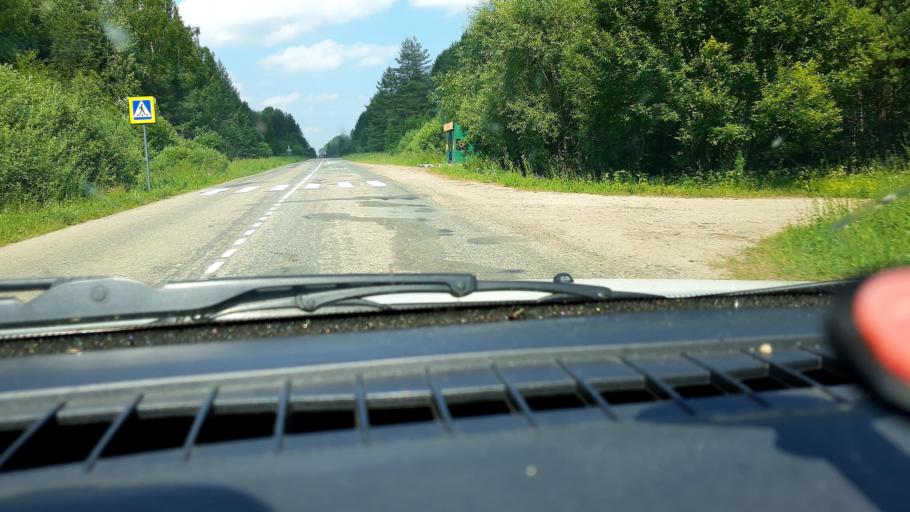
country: RU
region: Nizjnij Novgorod
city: Sharanga
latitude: 57.1040
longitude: 46.5298
